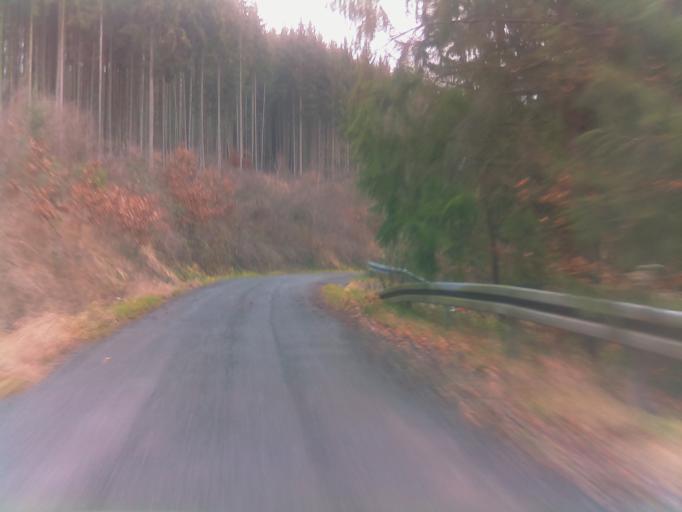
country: DE
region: Thuringia
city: Herschdorf
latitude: 50.7053
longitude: 11.4890
